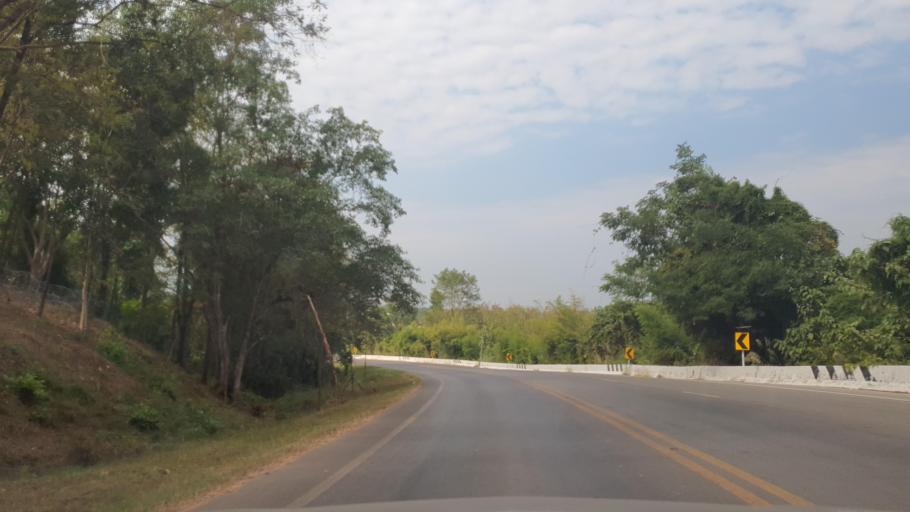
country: TH
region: Changwat Bueng Kan
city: Bung Khla
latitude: 18.2907
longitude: 103.8900
